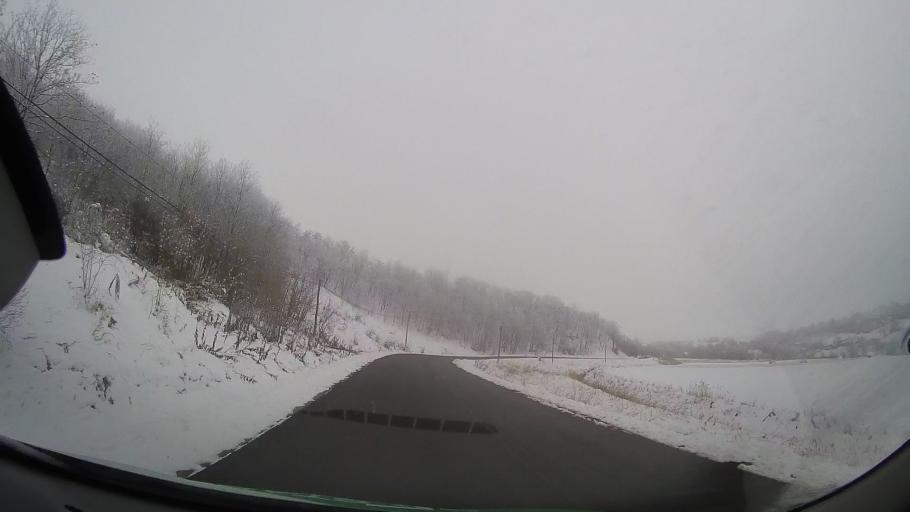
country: RO
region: Bacau
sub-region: Comuna Oncesti
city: Oncesti
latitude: 46.4769
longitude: 27.2572
